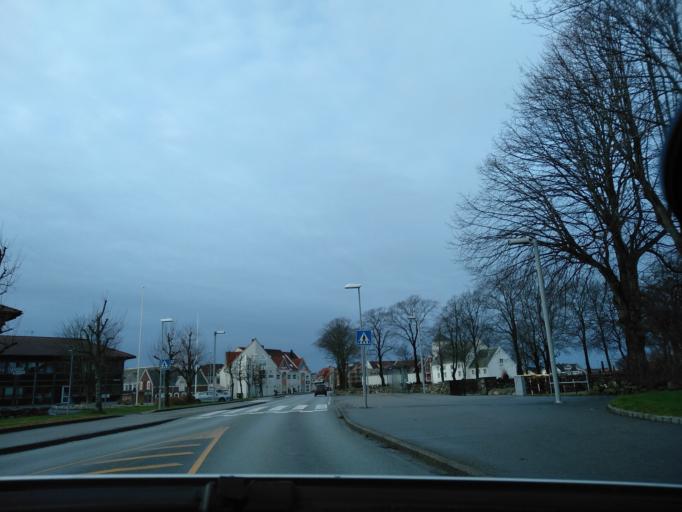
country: NO
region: Rogaland
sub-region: Randaberg
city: Randaberg
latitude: 58.9991
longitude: 5.6218
